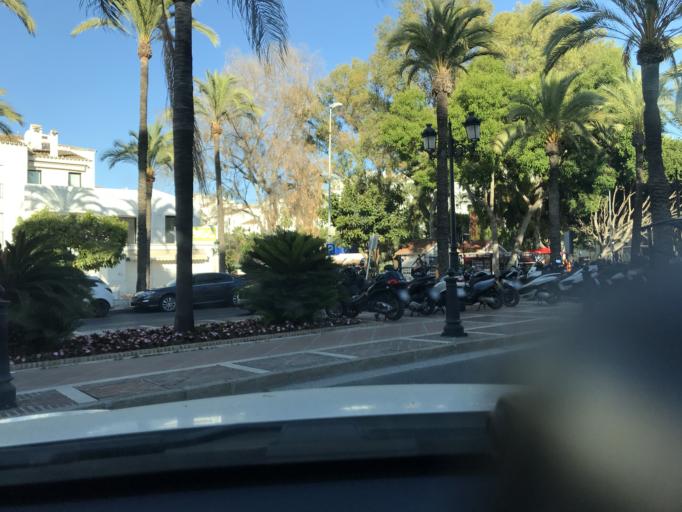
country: ES
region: Andalusia
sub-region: Provincia de Malaga
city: Marbella
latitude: 36.4871
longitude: -4.9559
